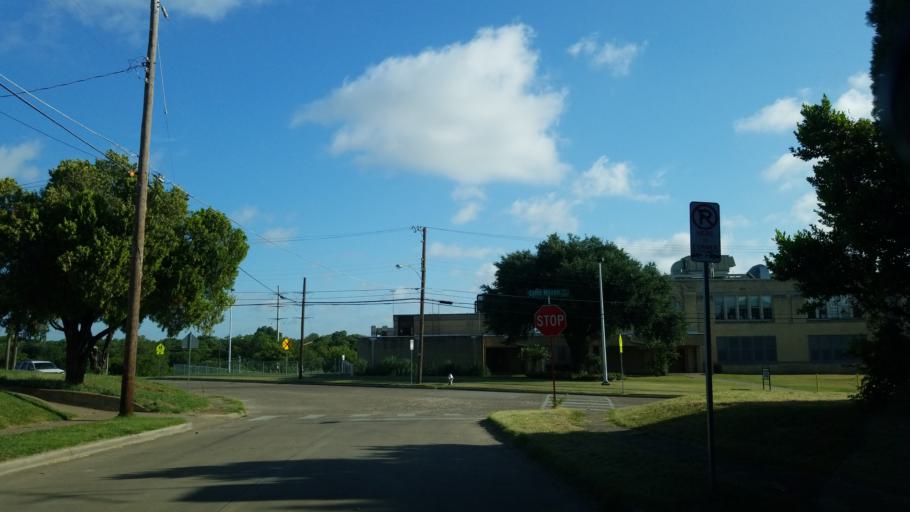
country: US
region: Texas
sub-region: Dallas County
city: Dallas
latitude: 32.7315
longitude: -96.8029
